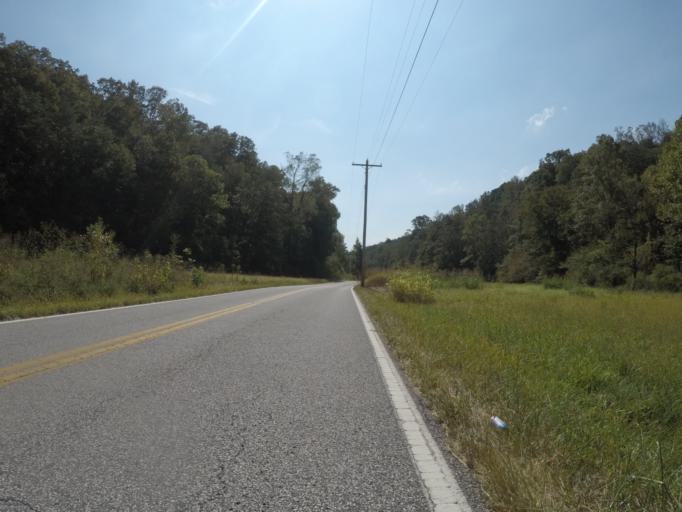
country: US
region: West Virginia
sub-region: Cabell County
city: Lesage
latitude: 38.5721
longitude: -82.4035
